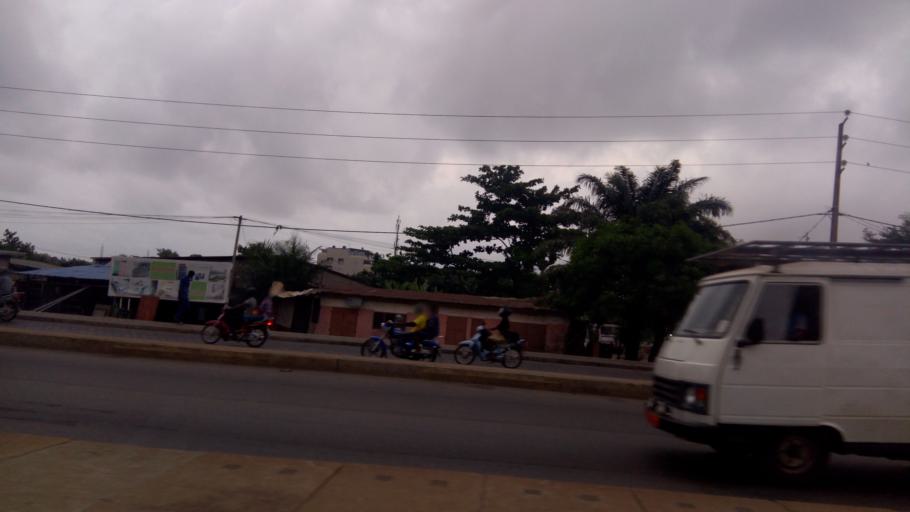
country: BJ
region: Littoral
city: Cotonou
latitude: 6.3875
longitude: 2.3684
